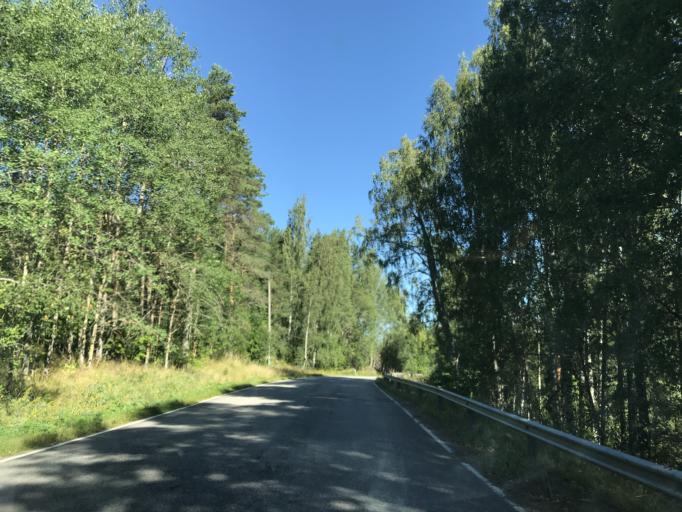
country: FI
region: Paijanne Tavastia
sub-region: Lahti
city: Orimattila
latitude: 60.7956
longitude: 25.6928
